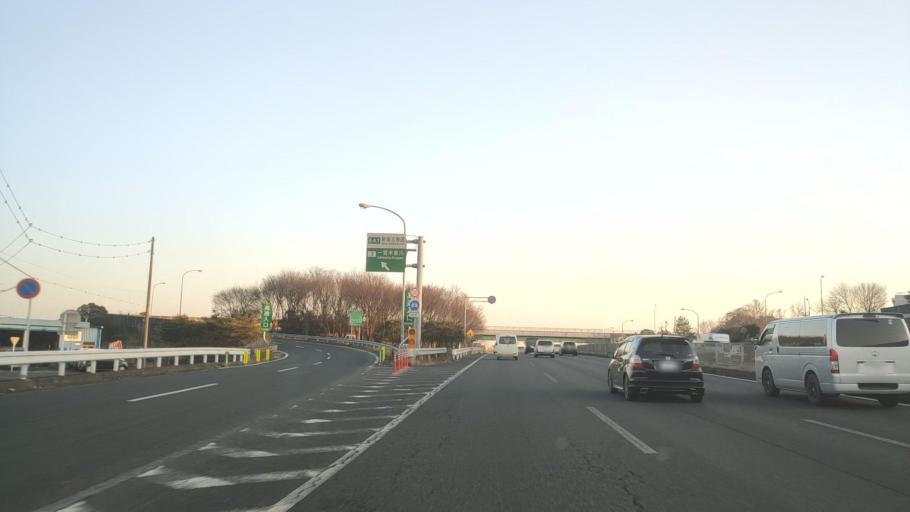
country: JP
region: Aichi
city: Kuroda
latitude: 35.3424
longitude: 136.7967
